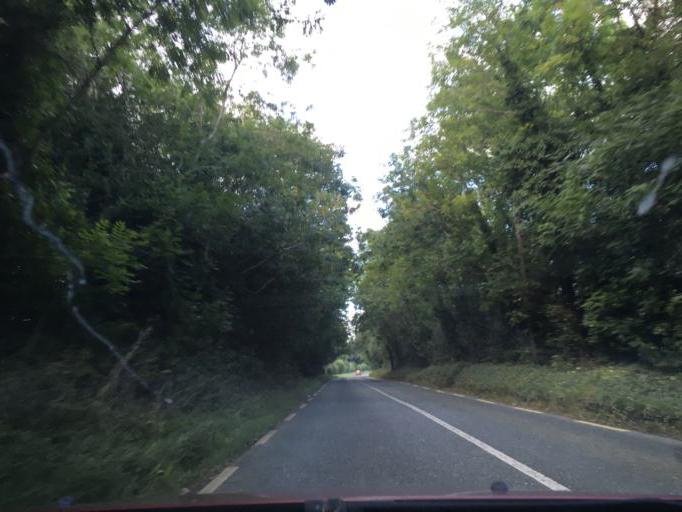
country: IE
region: Leinster
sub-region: Wicklow
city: Wicklow
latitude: 52.9572
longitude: -6.0699
